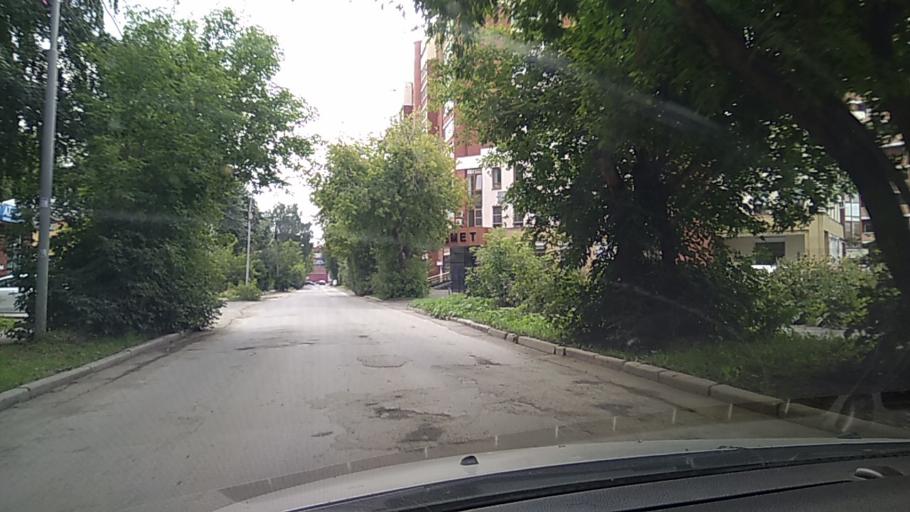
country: RU
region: Sverdlovsk
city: Yekaterinburg
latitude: 56.8804
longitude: 60.6198
